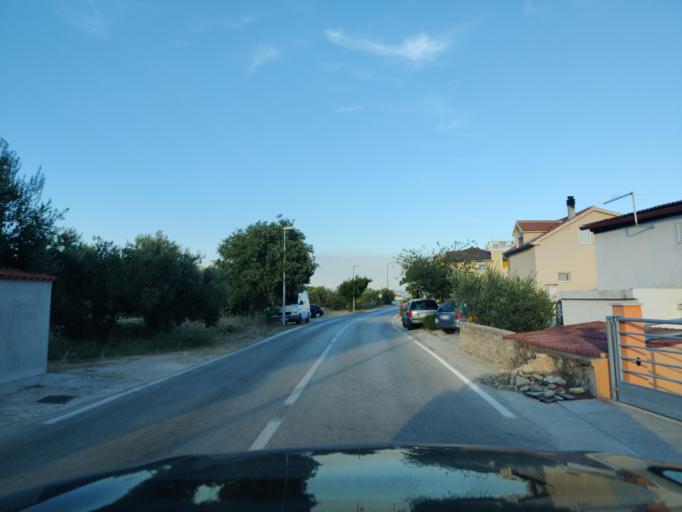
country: HR
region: Sibensko-Kniniska
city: Tribunj
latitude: 43.7594
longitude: 15.7518
